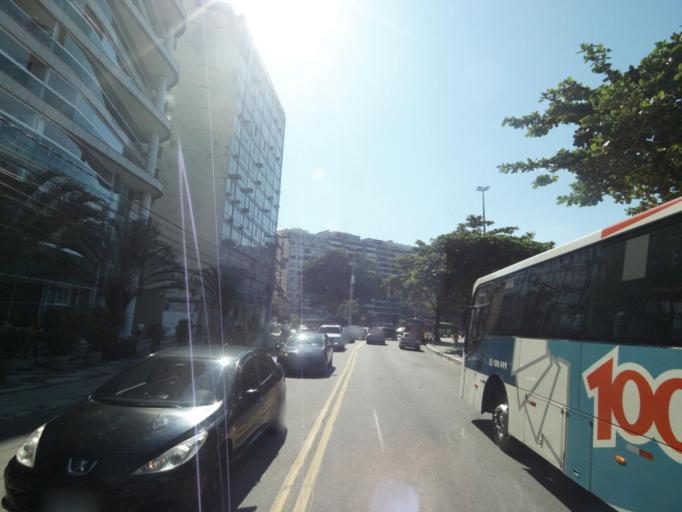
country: BR
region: Rio de Janeiro
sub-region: Niteroi
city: Niteroi
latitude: -22.9040
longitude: -43.1172
